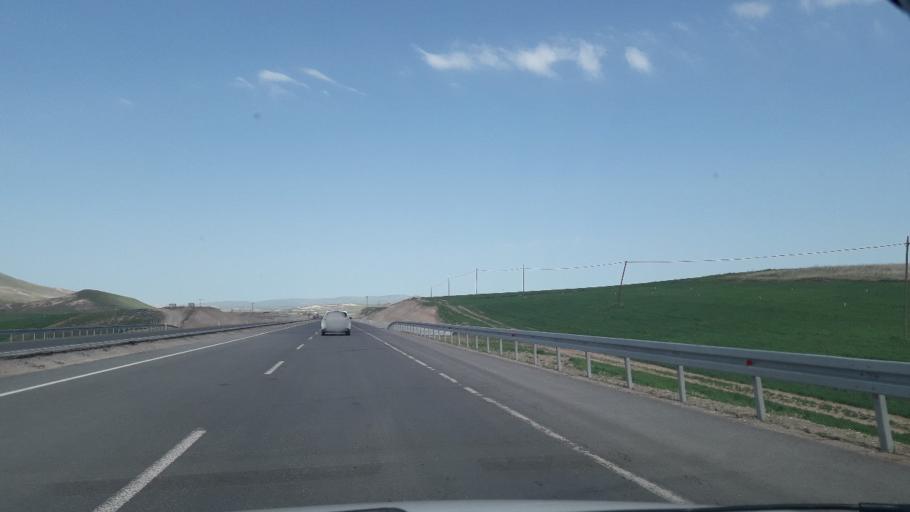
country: TR
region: Sivas
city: Deliktas
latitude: 39.2051
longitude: 37.2154
